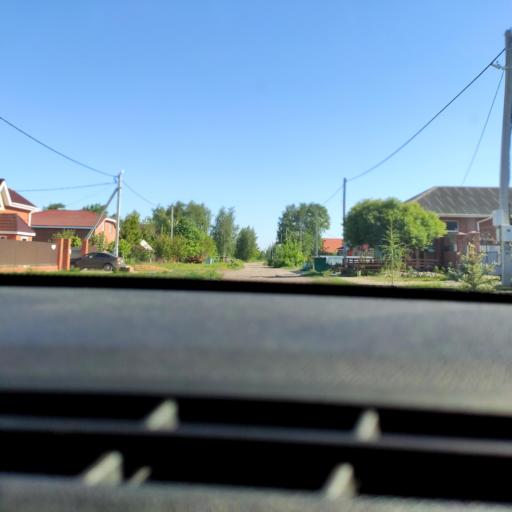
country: RU
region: Samara
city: Tol'yatti
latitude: 53.5569
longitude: 49.4091
